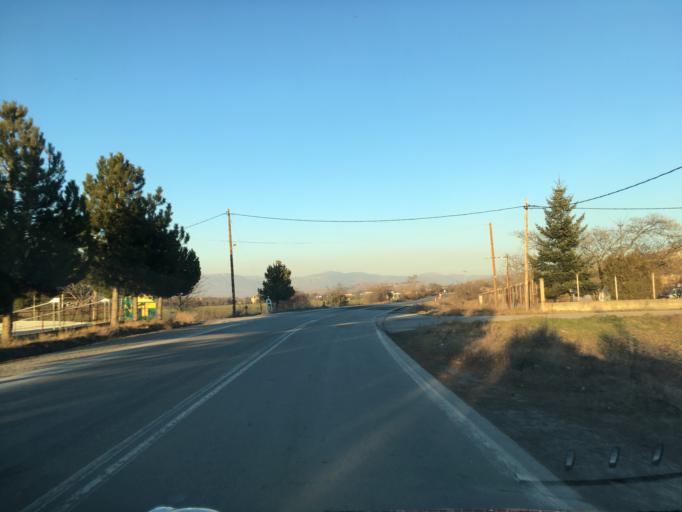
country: GR
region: West Macedonia
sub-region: Nomos Kozanis
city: Koila
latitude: 40.3243
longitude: 21.7769
